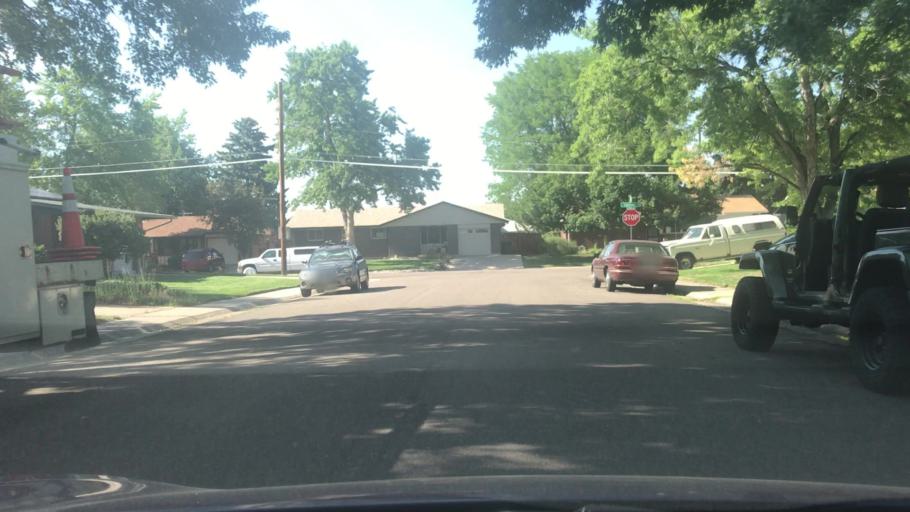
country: US
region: Colorado
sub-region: Arapahoe County
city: Glendale
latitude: 39.6922
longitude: -104.9102
